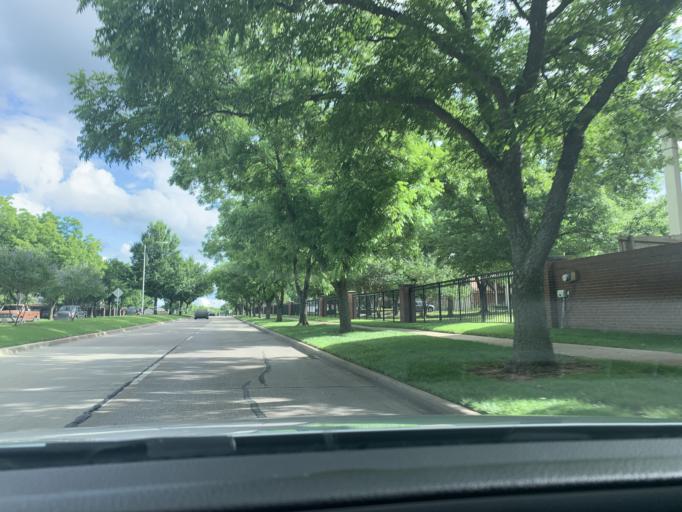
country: US
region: Texas
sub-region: Dallas County
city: Grand Prairie
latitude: 32.6645
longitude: -97.0022
